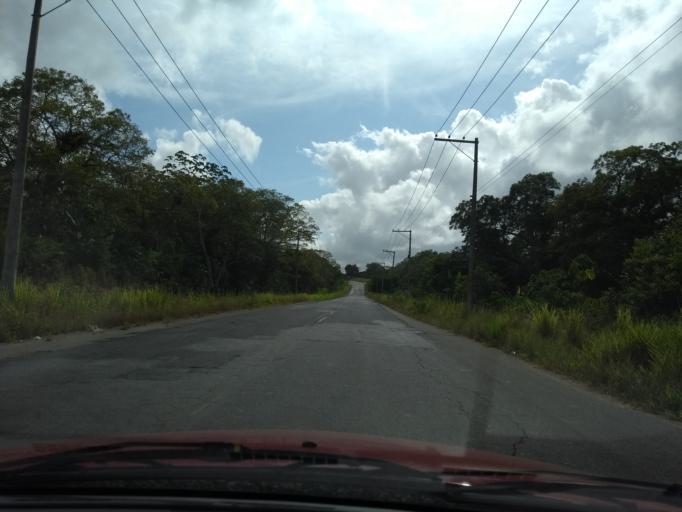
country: BR
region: Bahia
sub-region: Sao Francisco Do Conde
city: Sao Francisco do Conde
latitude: -12.6102
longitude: -38.6488
